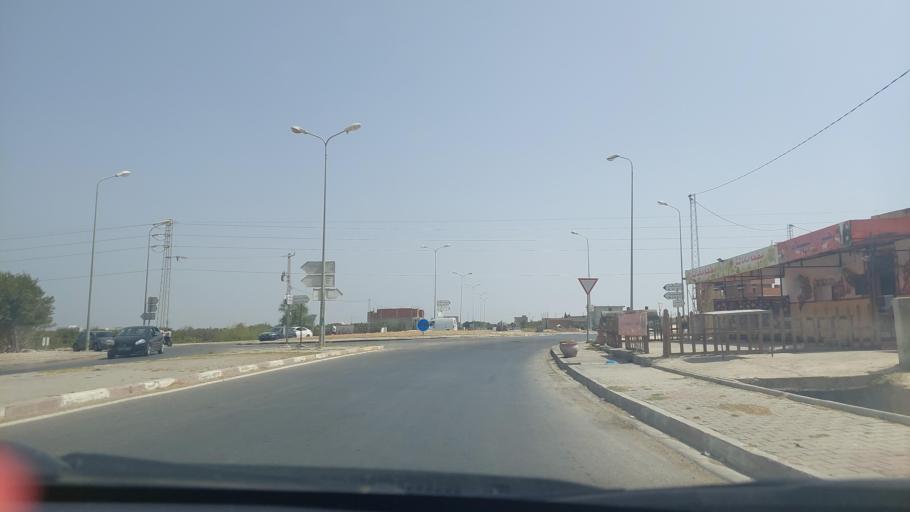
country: TN
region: Al Munastir
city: Qasr Hallal
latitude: 35.6041
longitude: 10.8901
